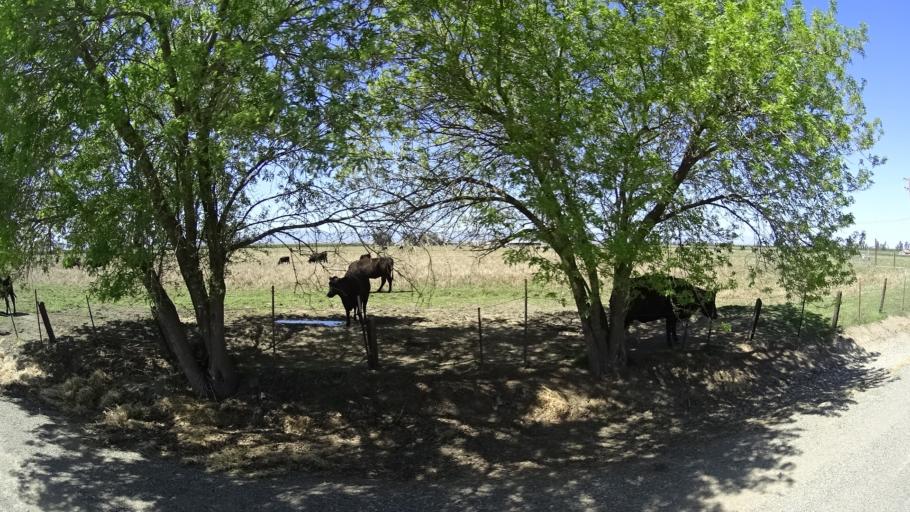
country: US
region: California
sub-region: Glenn County
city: Willows
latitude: 39.6300
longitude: -122.2347
